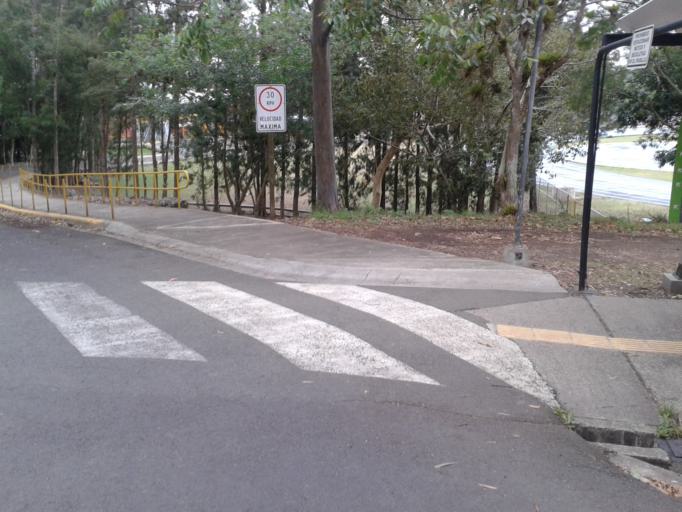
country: CR
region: Cartago
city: Cartago
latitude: 9.8559
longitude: -83.9105
